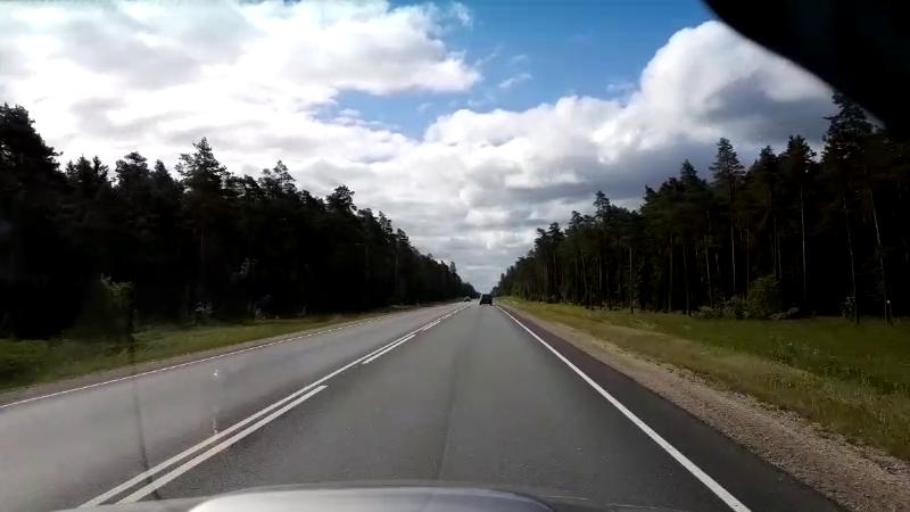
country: EE
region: Raplamaa
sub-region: Maerjamaa vald
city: Marjamaa
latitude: 59.0177
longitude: 24.4523
